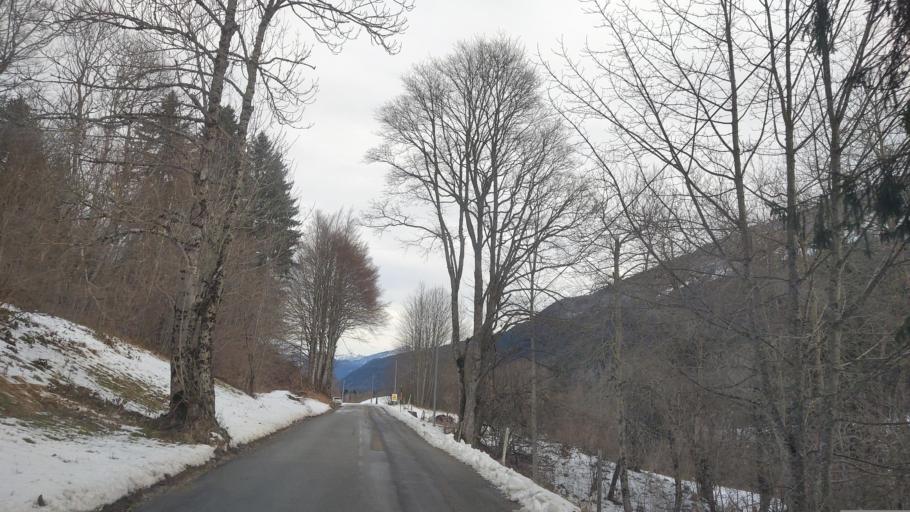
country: FR
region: Rhone-Alpes
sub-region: Departement de la Savoie
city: Mery
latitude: 45.6487
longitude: 6.0214
